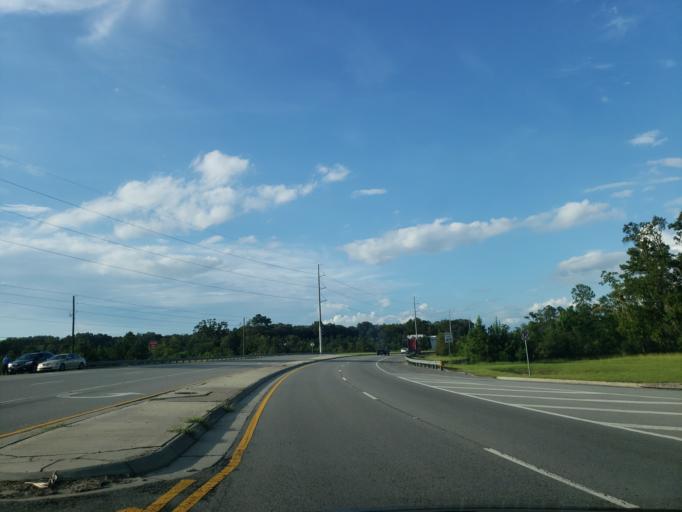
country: US
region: Georgia
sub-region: Chatham County
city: Georgetown
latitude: 32.0473
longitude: -81.2145
